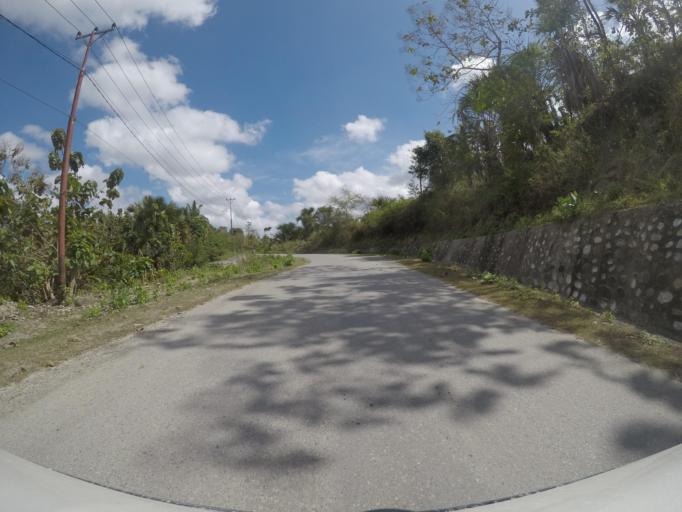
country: TL
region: Viqueque
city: Viqueque
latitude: -8.8715
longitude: 126.3519
